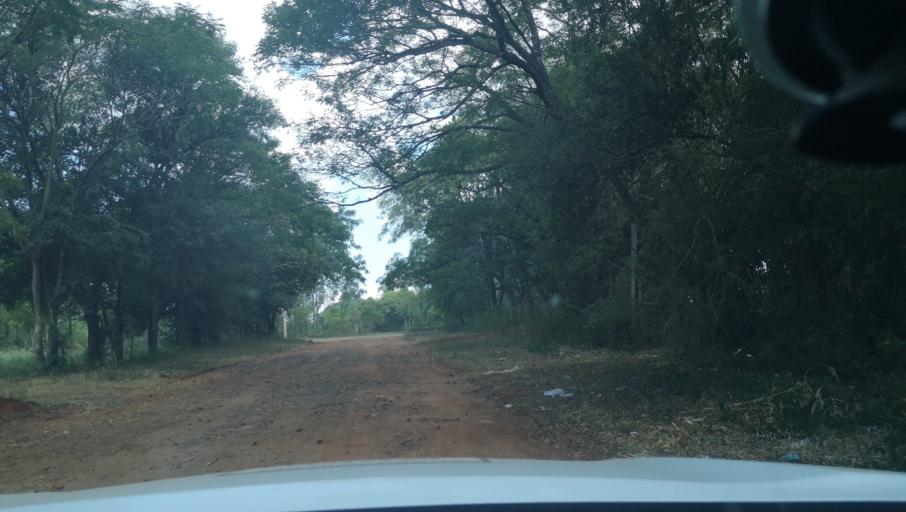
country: PY
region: Itapua
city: Carmen del Parana
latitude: -27.1569
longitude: -56.2474
